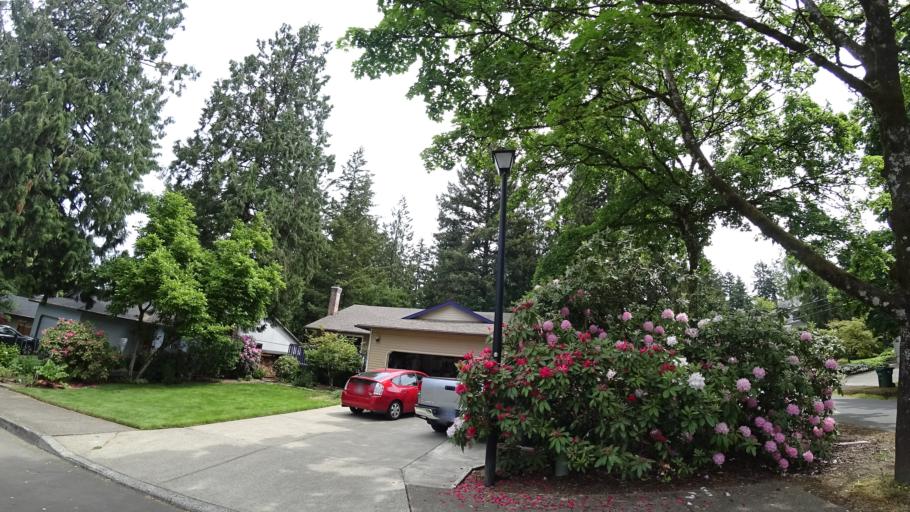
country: US
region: Oregon
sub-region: Washington County
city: Metzger
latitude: 45.4478
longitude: -122.7552
